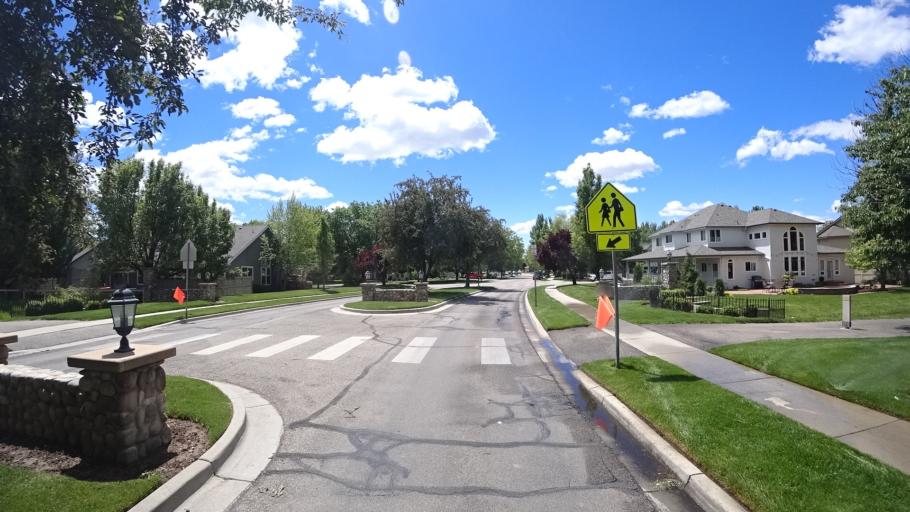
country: US
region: Idaho
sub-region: Ada County
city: Eagle
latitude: 43.6593
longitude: -116.3478
